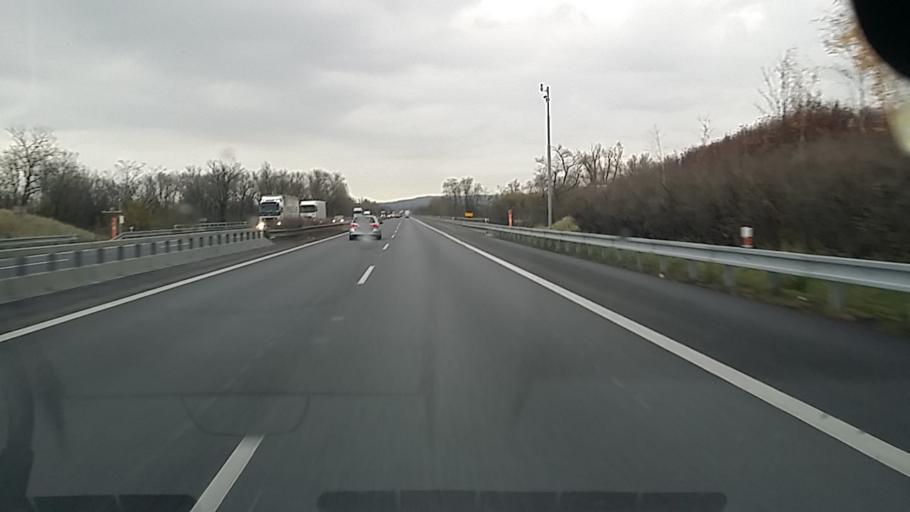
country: CZ
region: Central Bohemia
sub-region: Okres Melnik
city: Veltrusy
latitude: 50.3063
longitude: 14.3228
